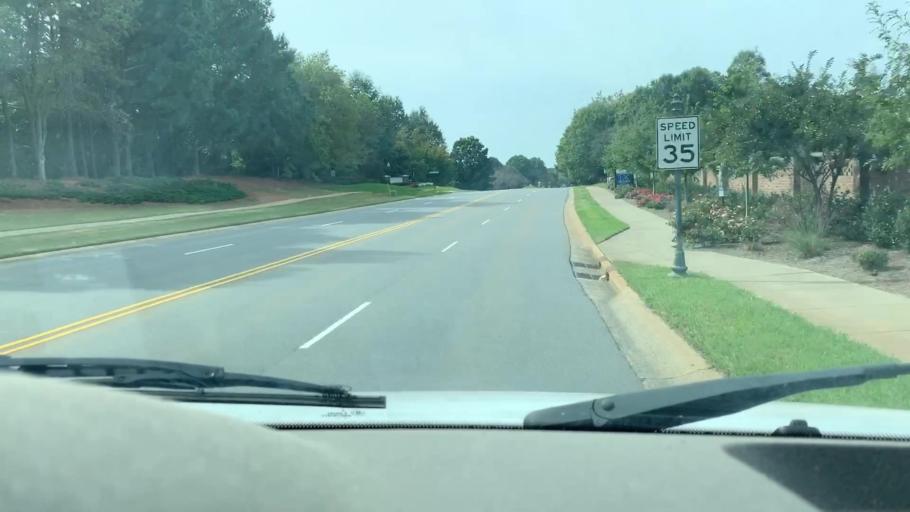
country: US
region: North Carolina
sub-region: Mecklenburg County
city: Cornelius
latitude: 35.4767
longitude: -80.8950
